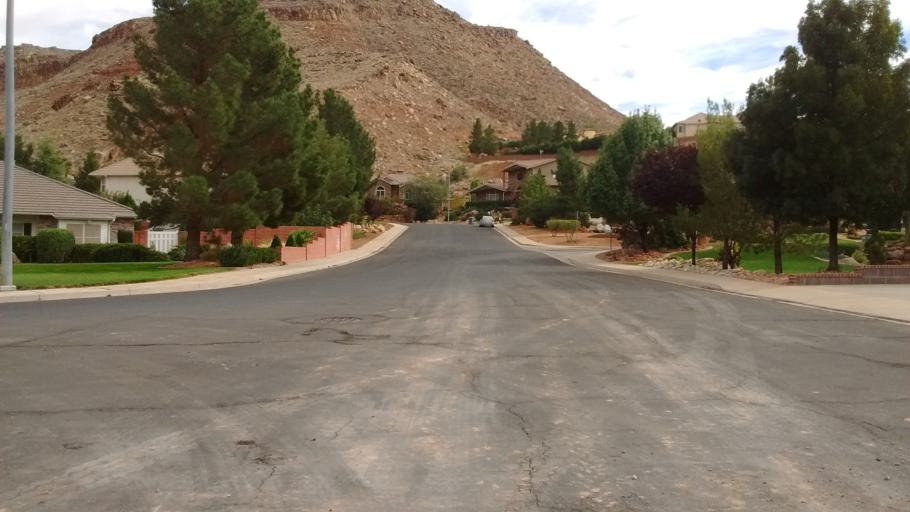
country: US
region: Utah
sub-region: Washington County
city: Washington
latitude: 37.1219
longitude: -113.4945
